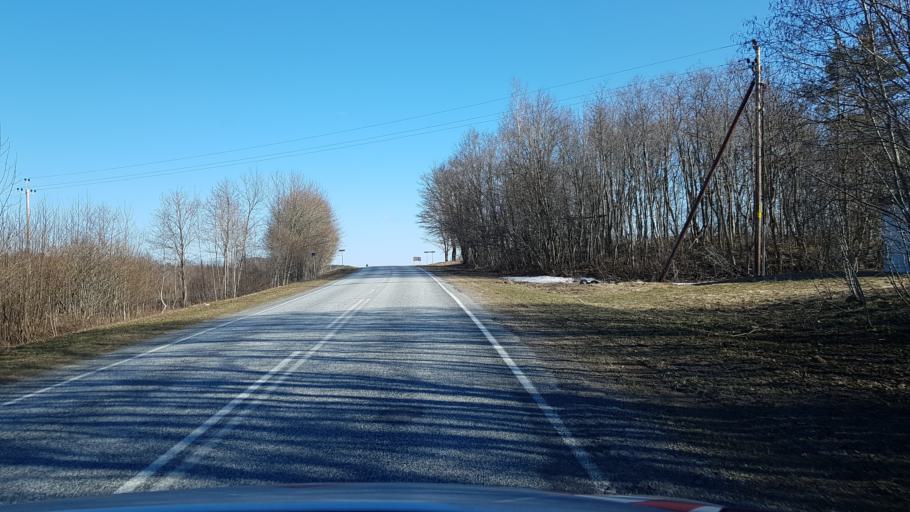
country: EE
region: Laeaene-Virumaa
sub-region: Haljala vald
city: Haljala
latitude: 59.4763
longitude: 26.1605
